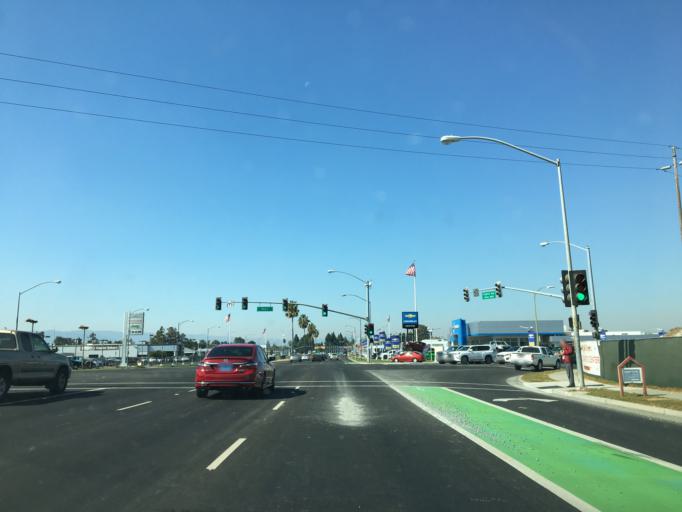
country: US
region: California
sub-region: Santa Clara County
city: Seven Trees
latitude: 37.2753
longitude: -121.8699
